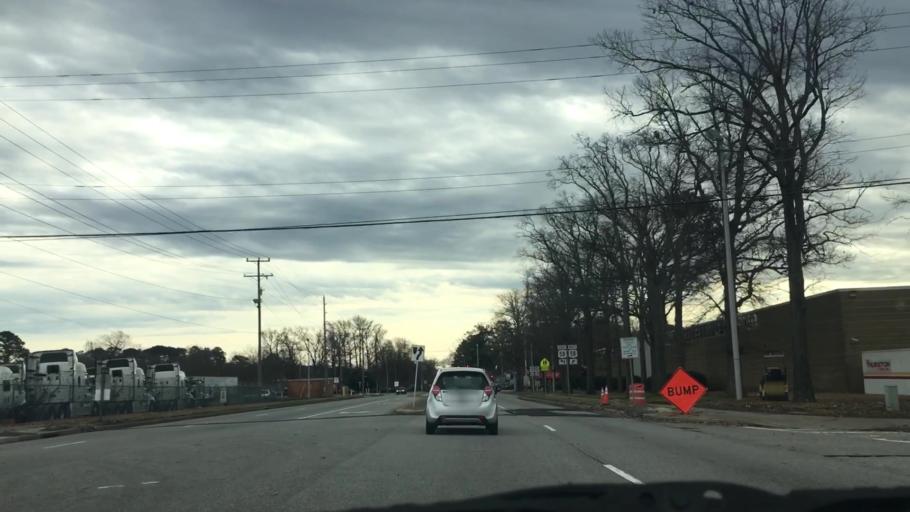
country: US
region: Virginia
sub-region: City of Norfolk
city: Norfolk
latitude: 36.8564
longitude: -76.2409
